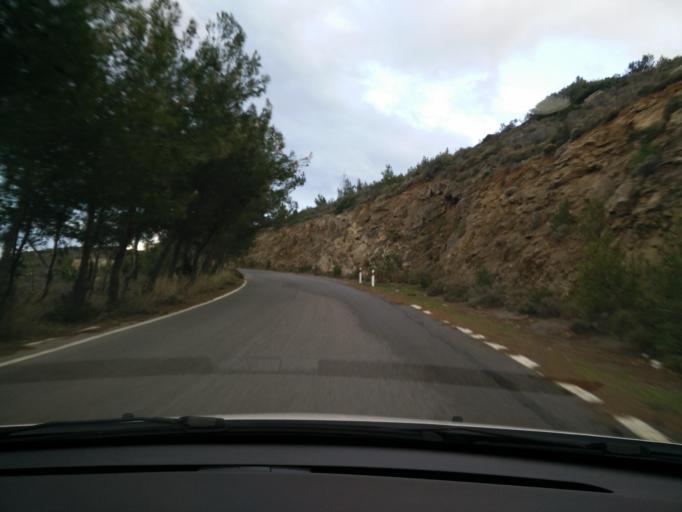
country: GR
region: Crete
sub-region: Nomos Lasithiou
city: Gra Liyia
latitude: 35.0887
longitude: 25.6999
